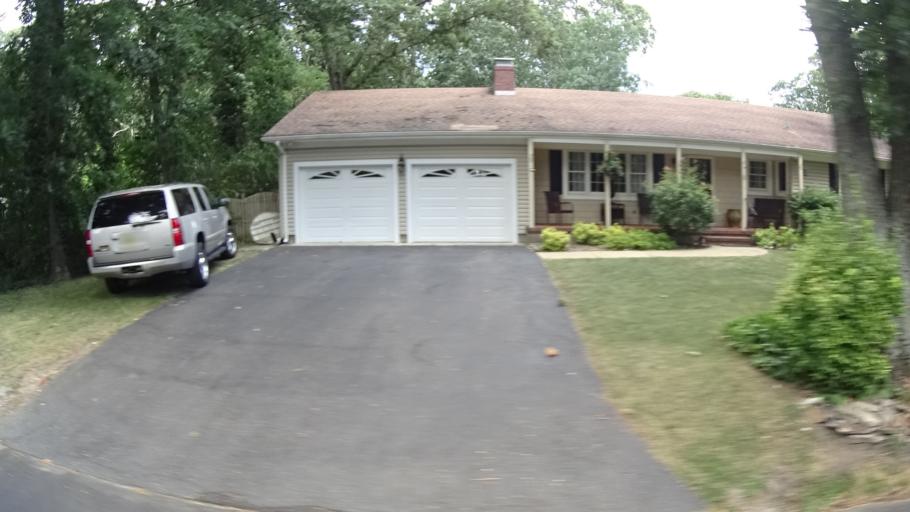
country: US
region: New Jersey
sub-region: Monmouth County
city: Brielle
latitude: 40.1067
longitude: -74.0853
